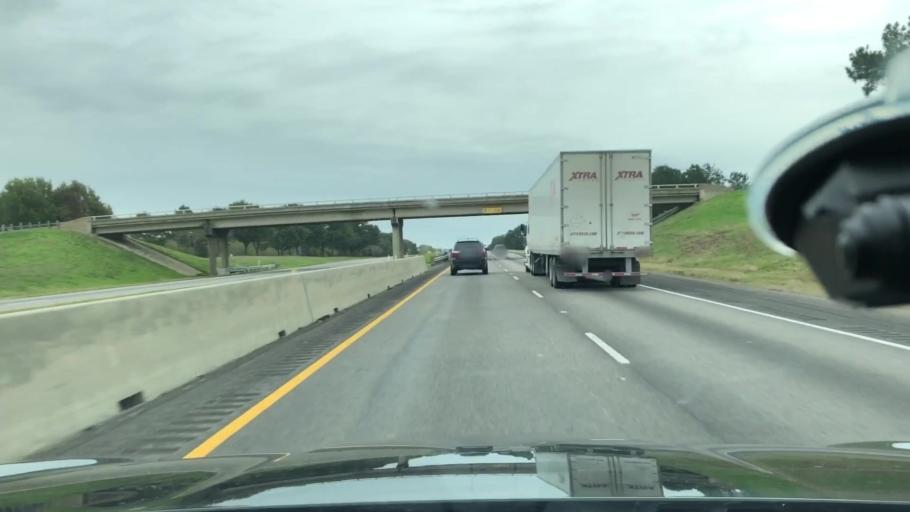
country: US
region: Texas
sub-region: Franklin County
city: Mount Vernon
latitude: 33.1661
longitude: -95.3819
